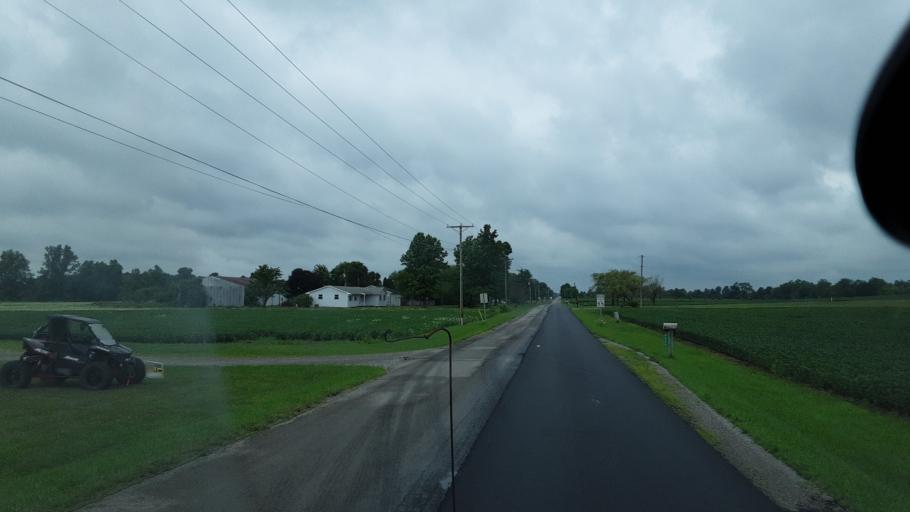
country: US
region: Indiana
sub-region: Allen County
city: New Haven
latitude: 40.9476
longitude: -85.0091
